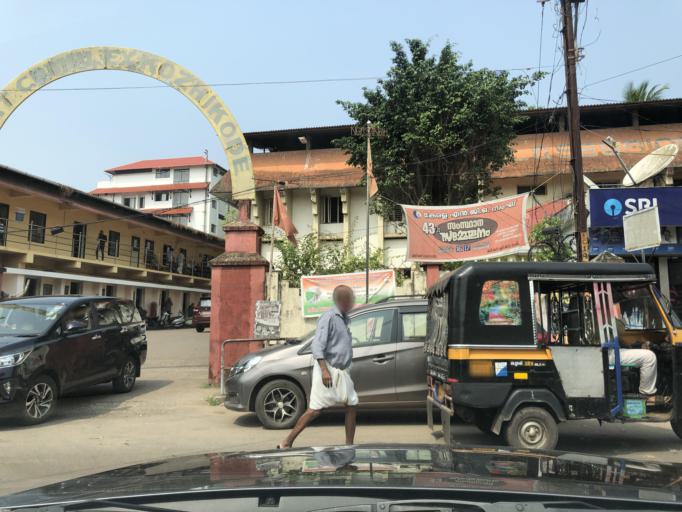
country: IN
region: Kerala
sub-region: Kozhikode
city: Kozhikode
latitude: 11.2514
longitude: 75.7755
